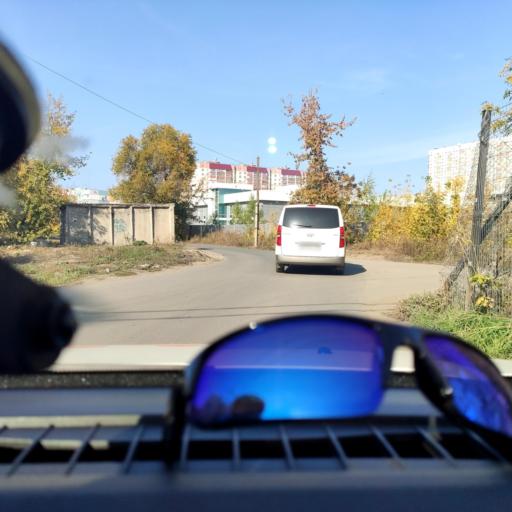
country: RU
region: Samara
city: Samara
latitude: 53.2495
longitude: 50.2135
